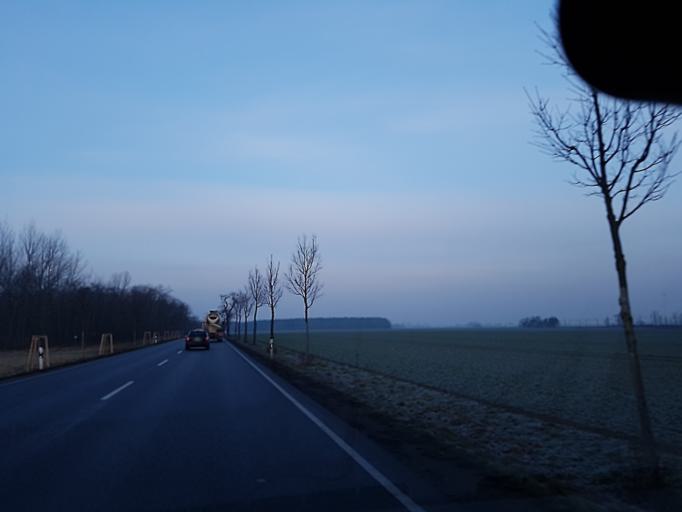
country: DE
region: Saxony-Anhalt
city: Elster
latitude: 51.8130
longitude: 12.8903
